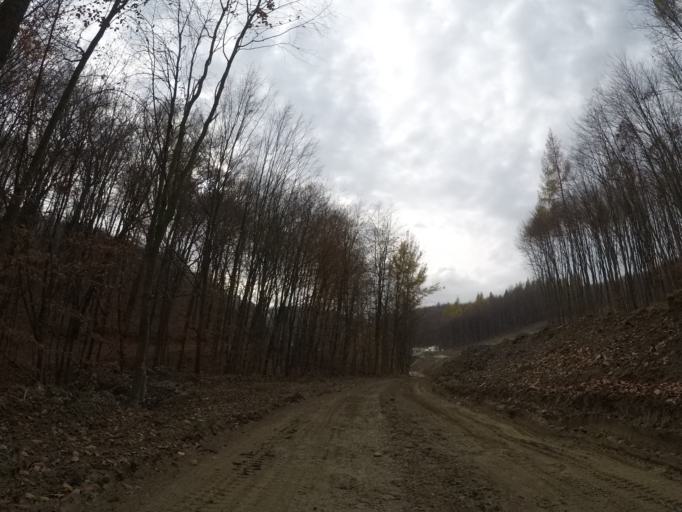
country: SK
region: Presovsky
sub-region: Okres Presov
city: Presov
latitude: 48.9798
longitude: 21.2169
